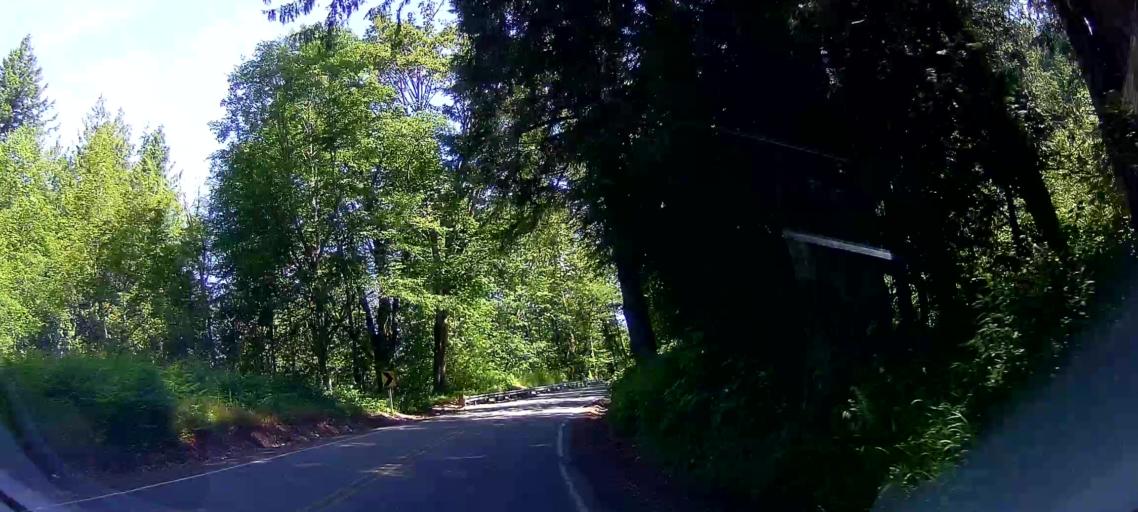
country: US
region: Washington
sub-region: Skagit County
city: Burlington
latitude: 48.5493
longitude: -122.3104
